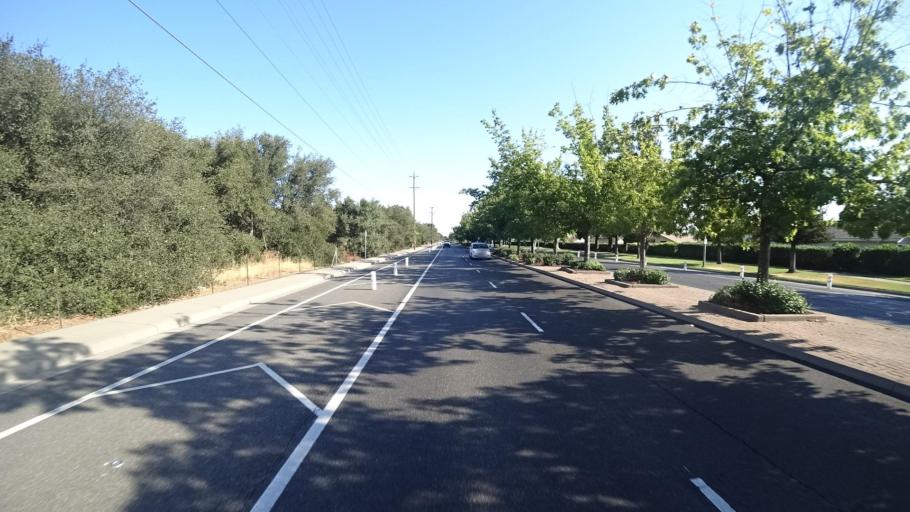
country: US
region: California
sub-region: Sacramento County
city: Laguna
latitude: 38.4392
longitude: -121.4468
